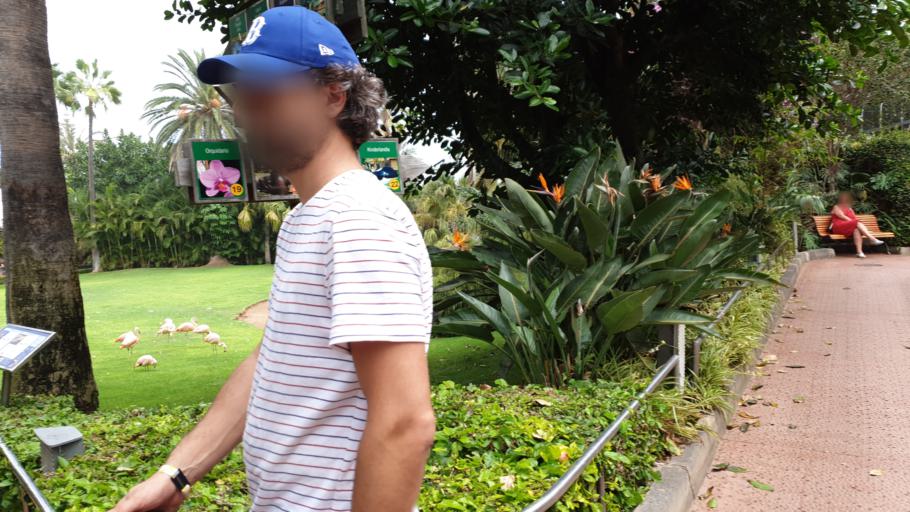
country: ES
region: Canary Islands
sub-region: Provincia de Santa Cruz de Tenerife
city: Puerto de la Cruz
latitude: 28.4091
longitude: -16.5638
